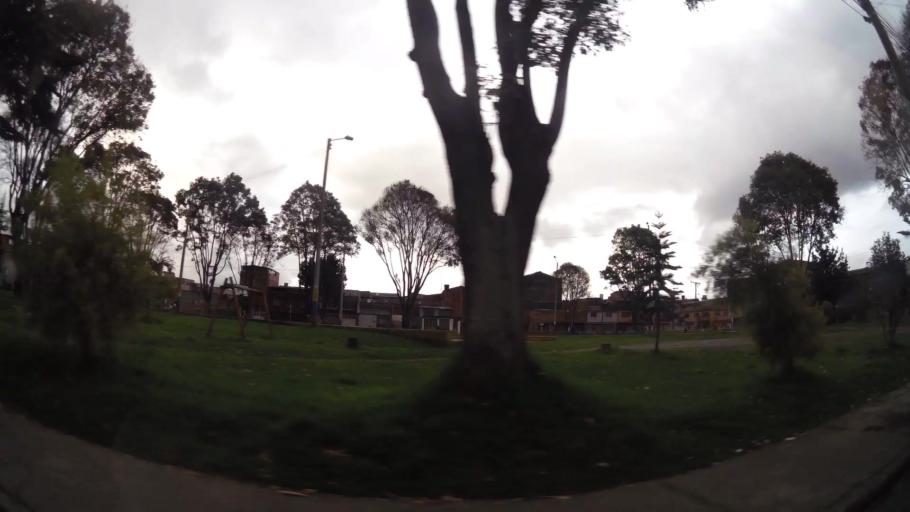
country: CO
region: Bogota D.C.
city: Bogota
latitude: 4.6828
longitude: -74.1025
